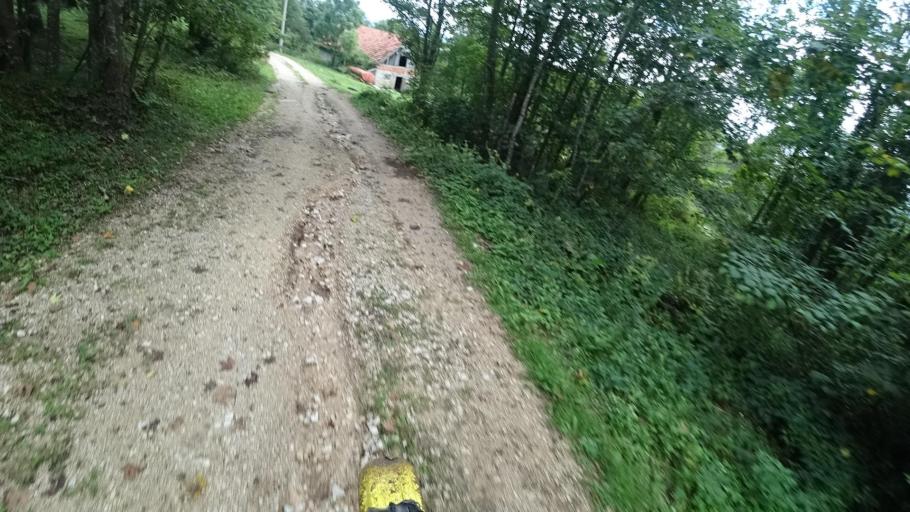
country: BA
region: Republika Srpska
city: Podbrdo
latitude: 44.5929
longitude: 17.0804
